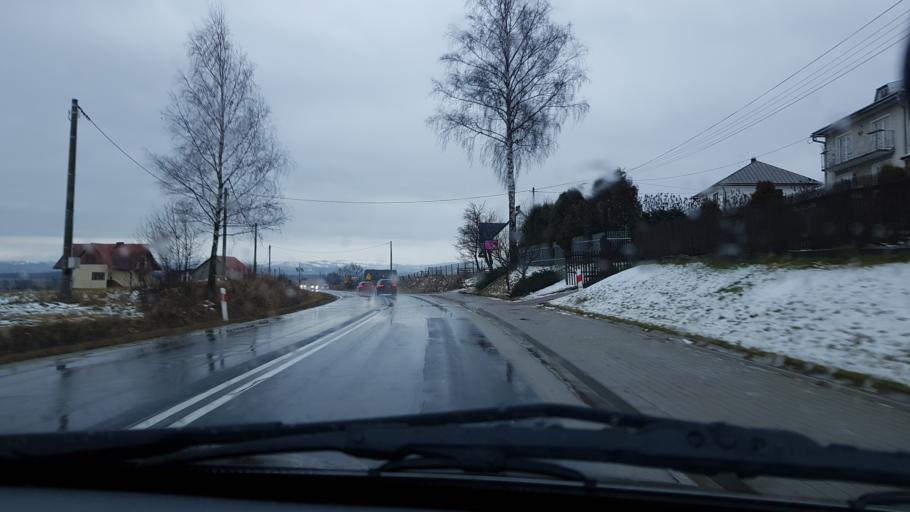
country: PL
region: Lesser Poland Voivodeship
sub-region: Powiat nowotarski
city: Czarny Dunajec
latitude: 49.4903
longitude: 19.8777
